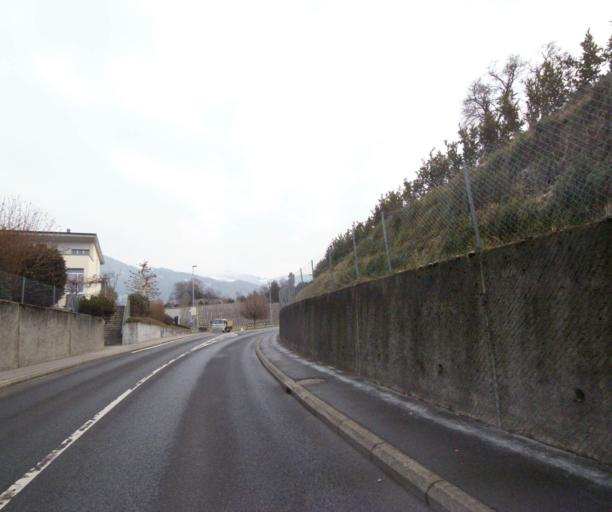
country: CH
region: Vaud
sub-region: Riviera-Pays-d'Enhaut District
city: La Tour-de-Peilz
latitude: 46.4614
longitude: 6.8678
